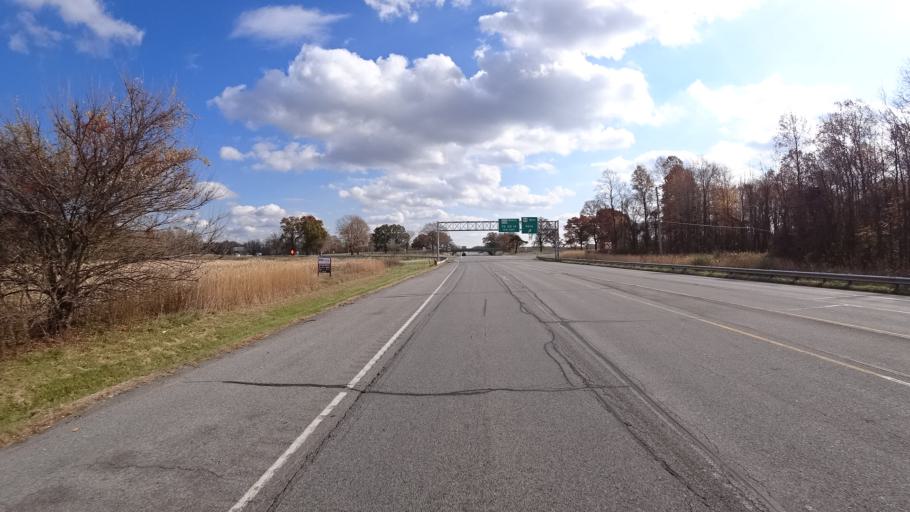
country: US
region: Indiana
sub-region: LaPorte County
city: Trail Creek
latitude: 41.6991
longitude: -86.8310
